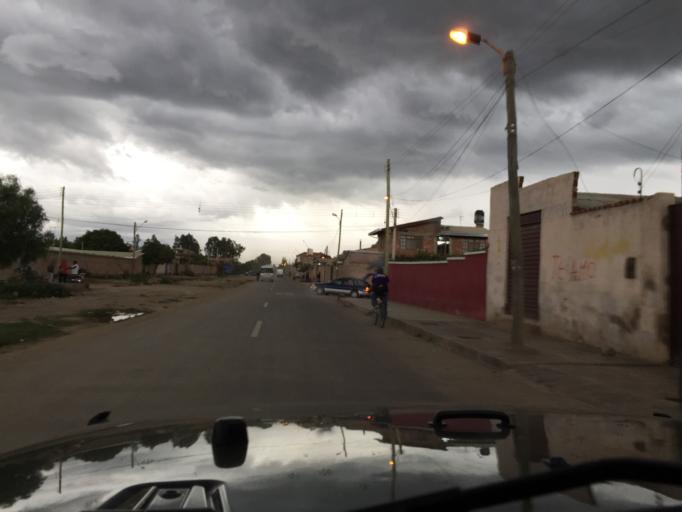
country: BO
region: Cochabamba
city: Cochabamba
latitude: -17.3997
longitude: -66.2122
